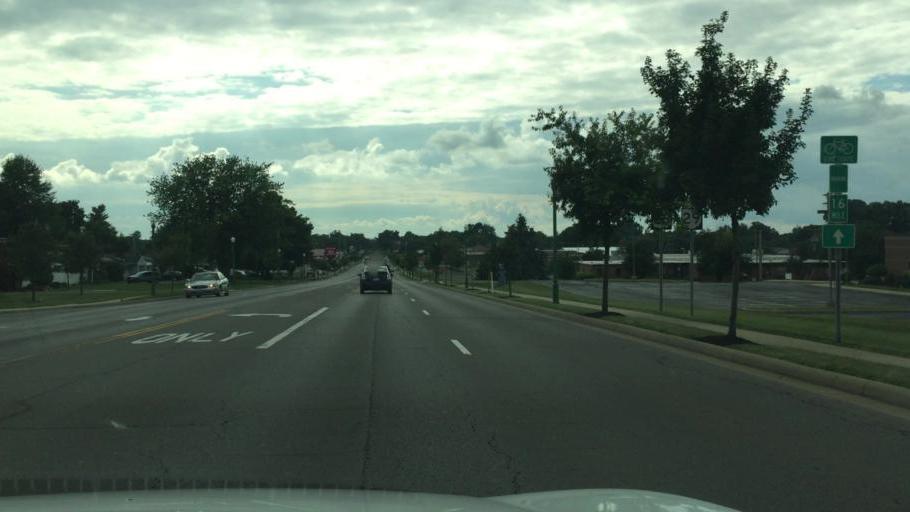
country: US
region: Ohio
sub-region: Champaign County
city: Urbana
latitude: 40.1067
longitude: -83.7302
